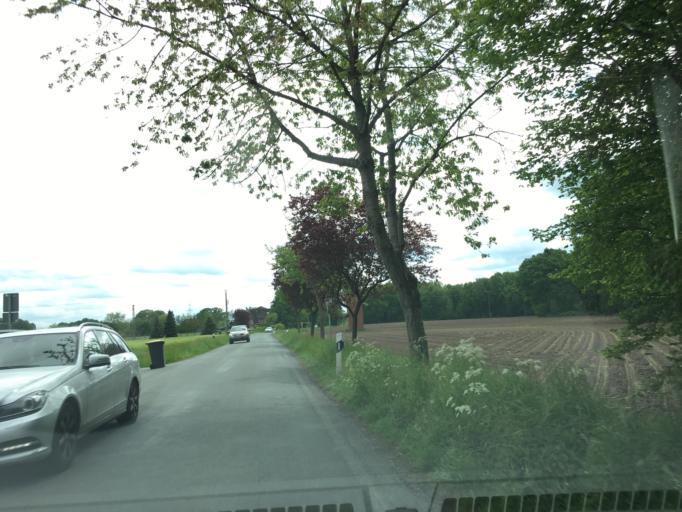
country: DE
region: North Rhine-Westphalia
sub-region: Regierungsbezirk Munster
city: Havixbeck
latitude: 51.9769
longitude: 7.4696
